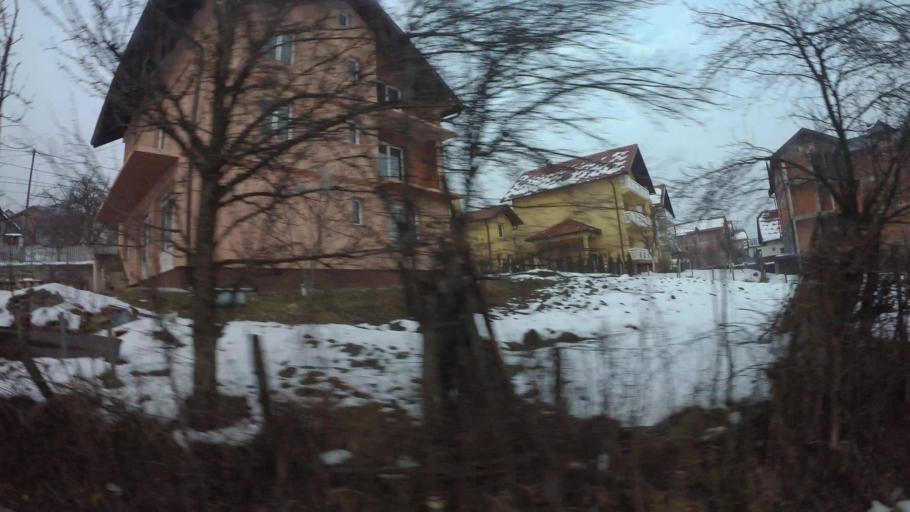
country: BA
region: Federation of Bosnia and Herzegovina
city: Vogosca
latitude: 43.9041
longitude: 18.3526
